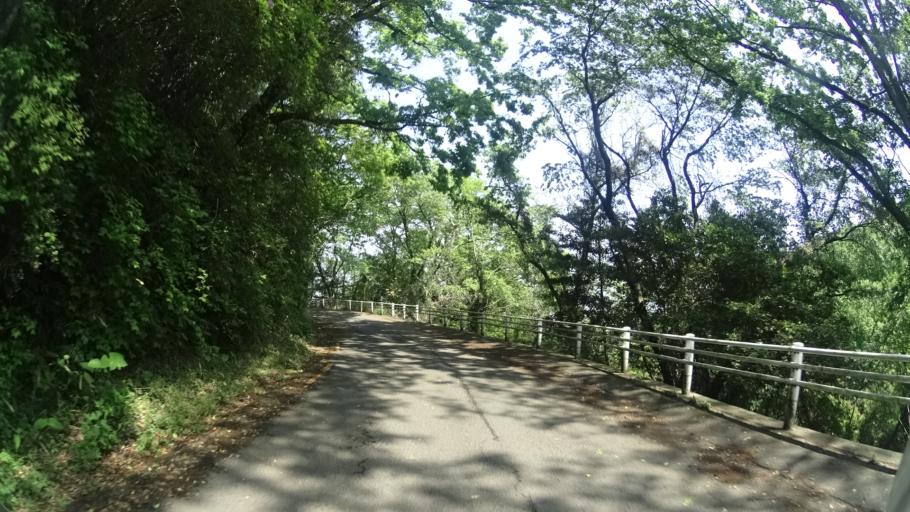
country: JP
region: Tokushima
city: Tokushima-shi
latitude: 34.0663
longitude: 134.5197
